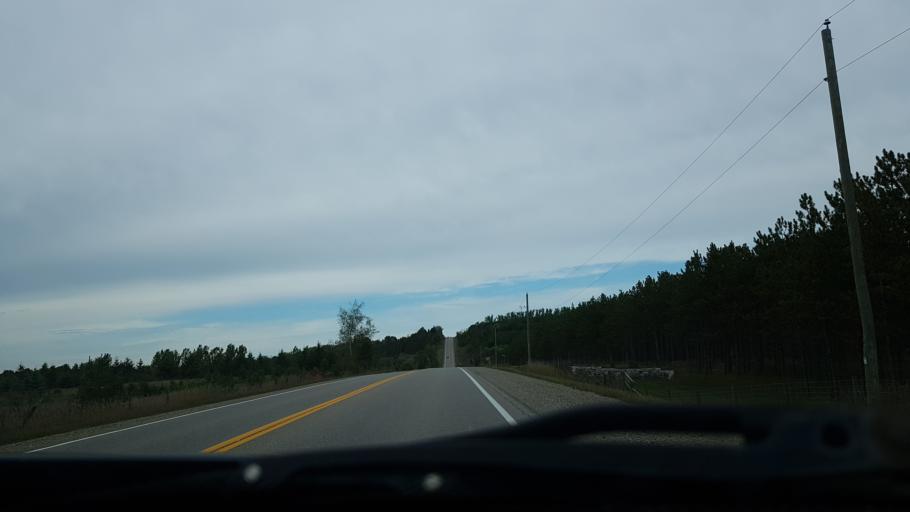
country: CA
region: Ontario
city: Shelburne
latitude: 44.0862
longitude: -80.0200
